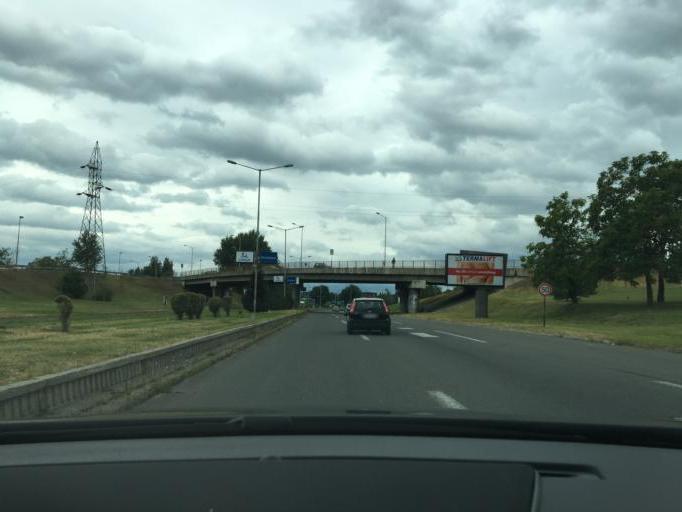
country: MK
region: Cair
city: Cair
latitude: 42.0022
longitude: 21.4904
